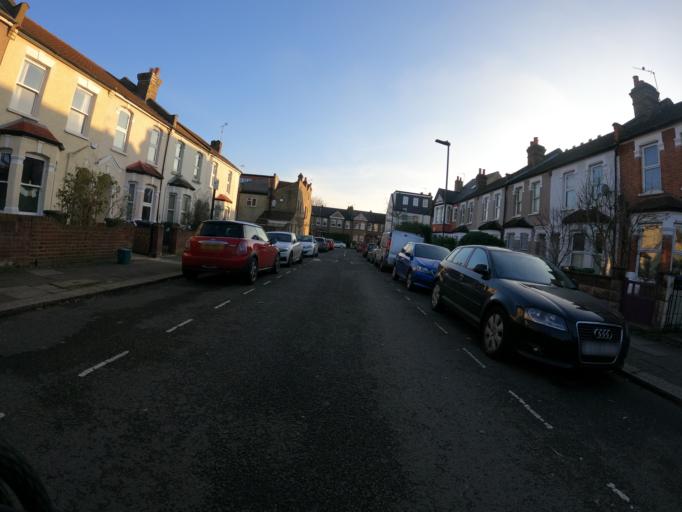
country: GB
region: England
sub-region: Greater London
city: Ealing
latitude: 51.5061
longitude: -0.3217
